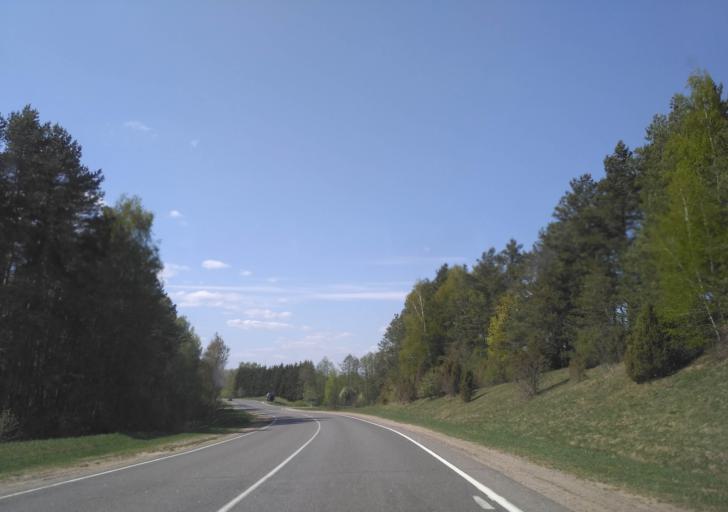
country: BY
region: Minsk
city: Narach
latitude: 54.8882
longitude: 26.7910
